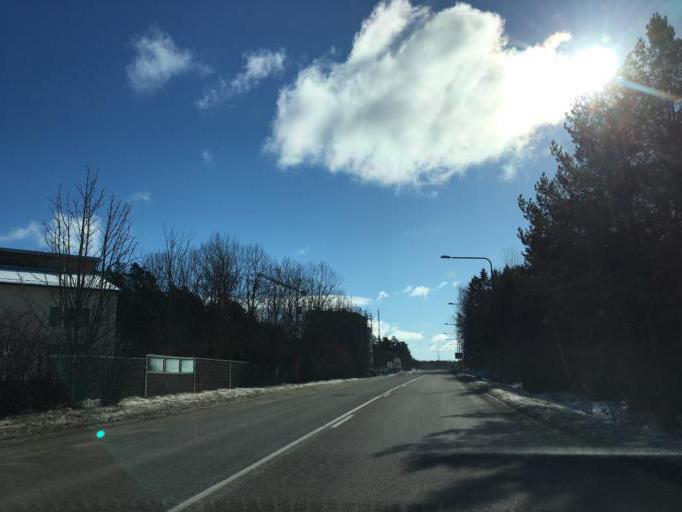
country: SE
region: Vaestmanland
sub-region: Vasteras
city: Vasteras
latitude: 59.6230
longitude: 16.4953
